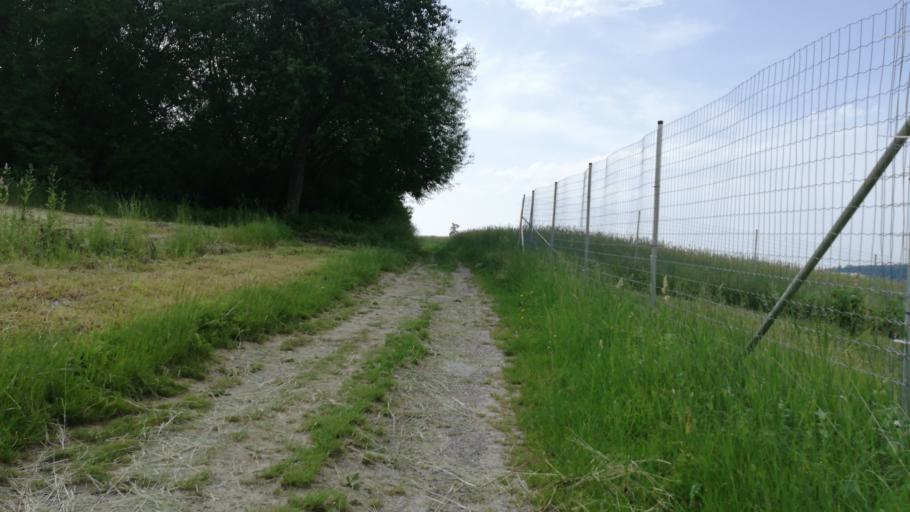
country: AT
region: Upper Austria
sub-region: Politischer Bezirk Grieskirchen
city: Bad Schallerbach
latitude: 48.2409
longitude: 13.9170
